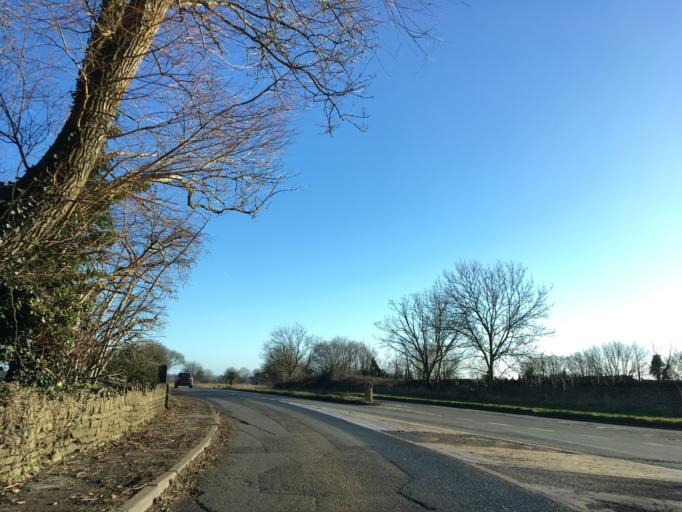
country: GB
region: England
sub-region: Wiltshire
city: Biddestone
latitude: 51.4726
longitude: -2.1705
